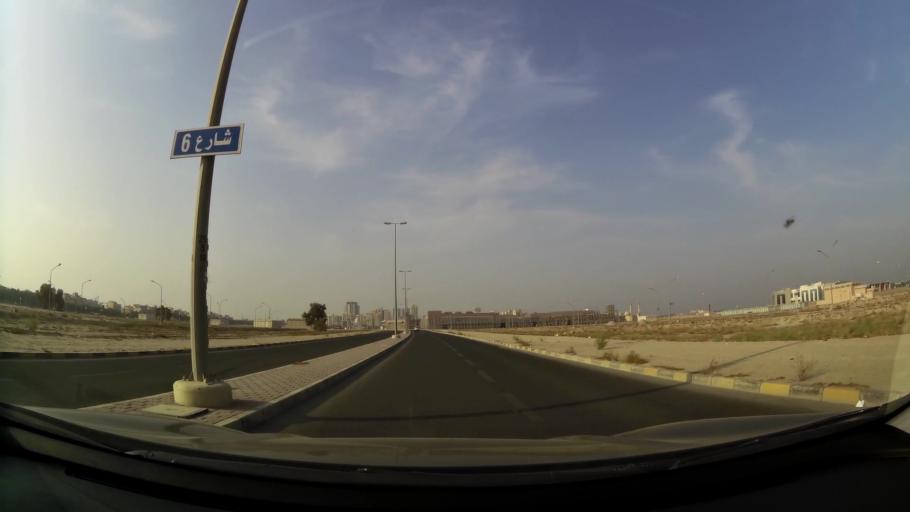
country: KW
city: Al Funaytis
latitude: 29.2384
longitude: 48.0874
